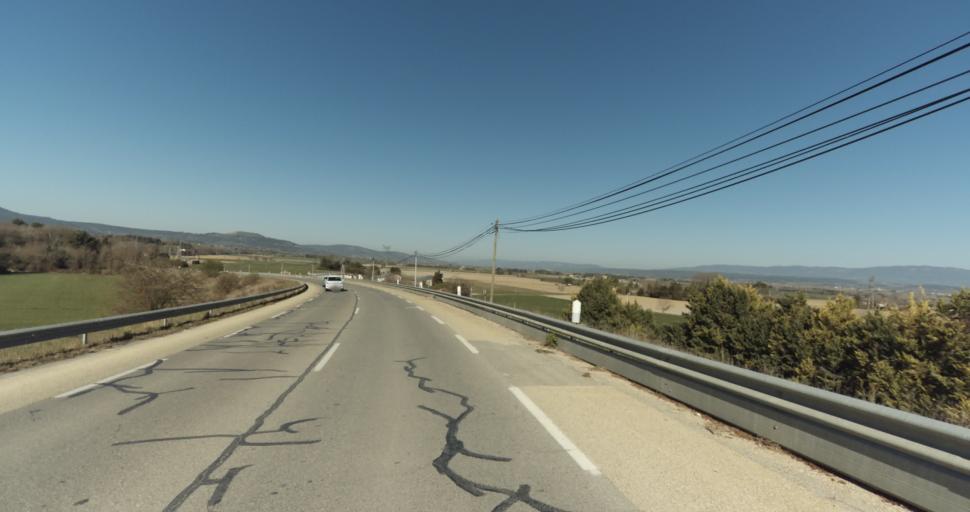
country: FR
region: Provence-Alpes-Cote d'Azur
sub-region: Departement des Bouches-du-Rhone
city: Meyrargues
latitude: 43.6436
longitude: 5.5214
